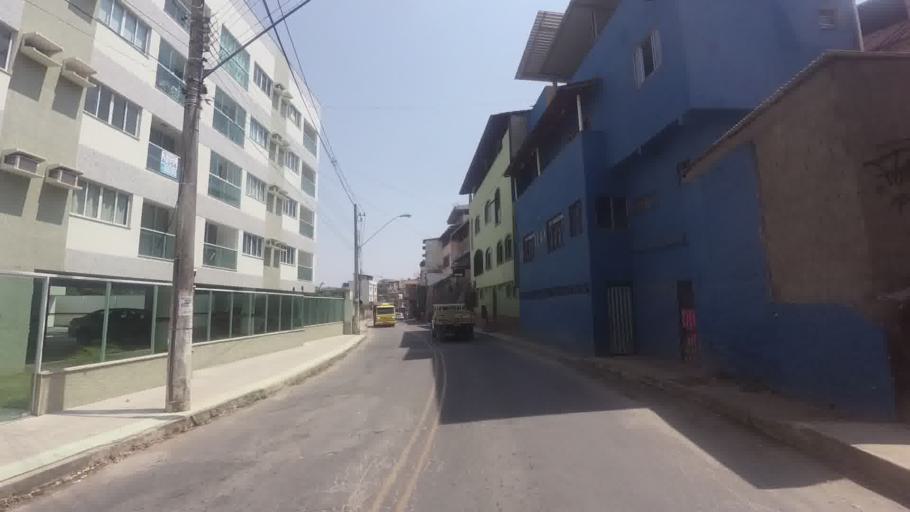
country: BR
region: Espirito Santo
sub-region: Cachoeiro De Itapemirim
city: Cachoeiro de Itapemirim
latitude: -20.8465
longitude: -41.1118
